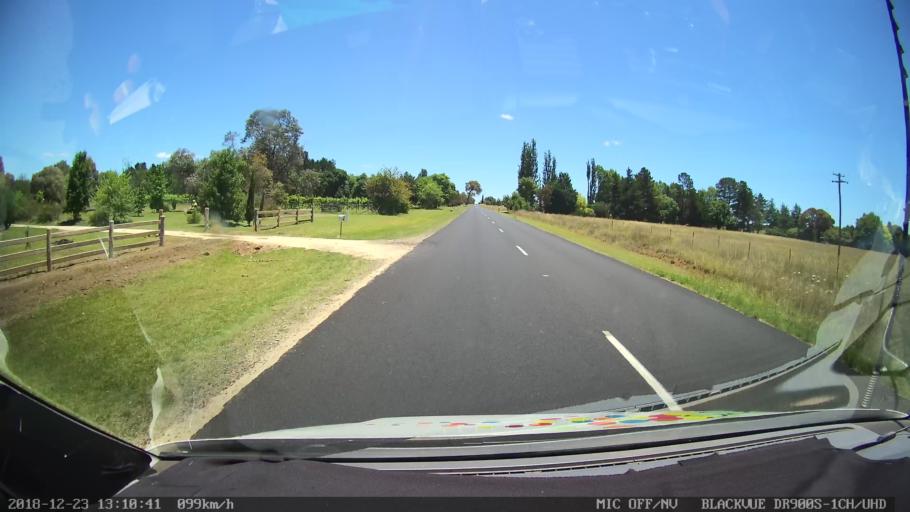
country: AU
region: New South Wales
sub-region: Armidale Dumaresq
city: Armidale
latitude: -30.5095
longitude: 151.5823
